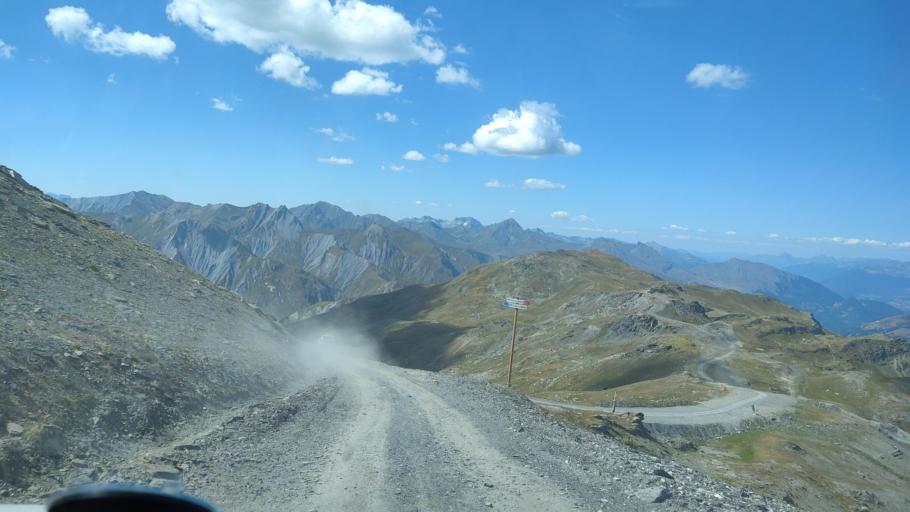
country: FR
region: Rhone-Alpes
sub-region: Departement de la Savoie
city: Val Thorens
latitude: 45.2989
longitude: 6.5069
